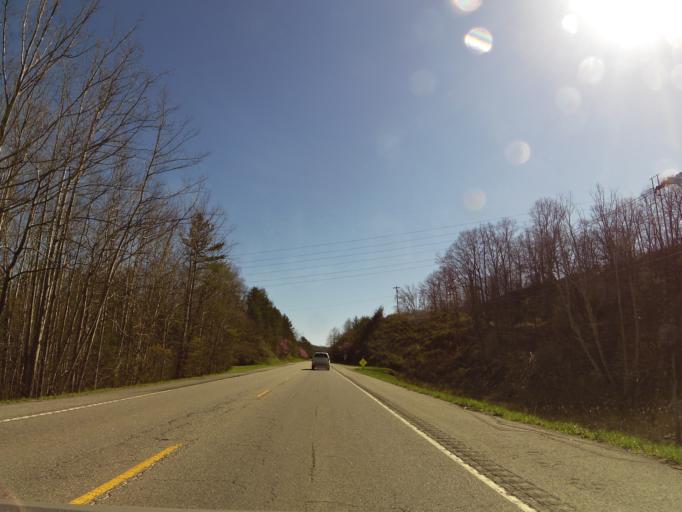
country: US
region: Tennessee
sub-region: Scott County
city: Oneida
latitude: 36.5472
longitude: -84.4545
